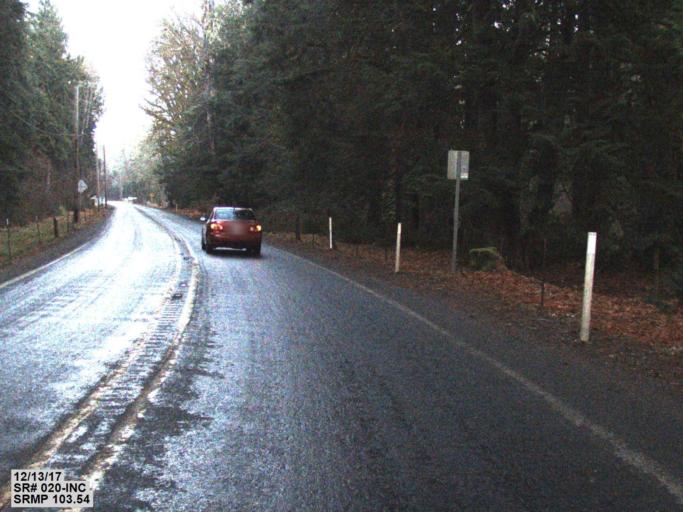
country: US
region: Washington
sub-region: Snohomish County
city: Darrington
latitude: 48.5091
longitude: -121.4718
